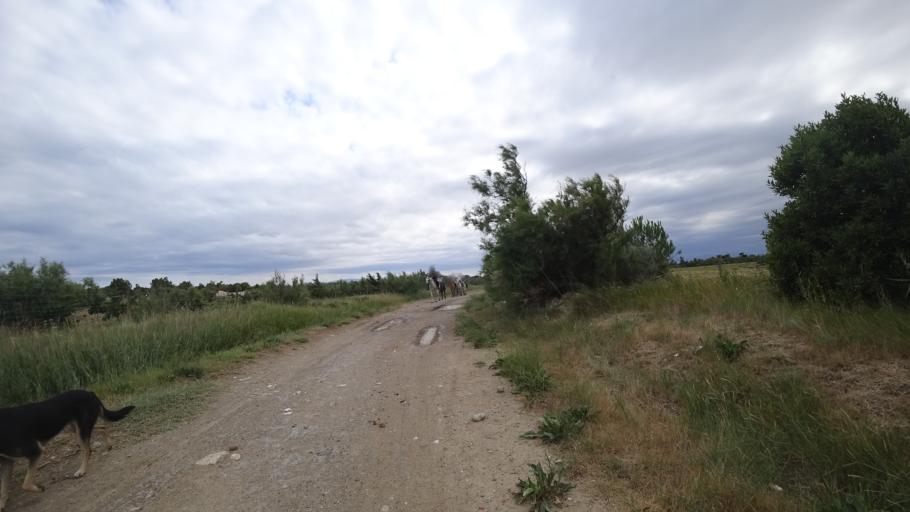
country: FR
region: Languedoc-Roussillon
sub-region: Departement des Pyrenees-Orientales
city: Le Barcares
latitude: 42.7815
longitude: 3.0198
